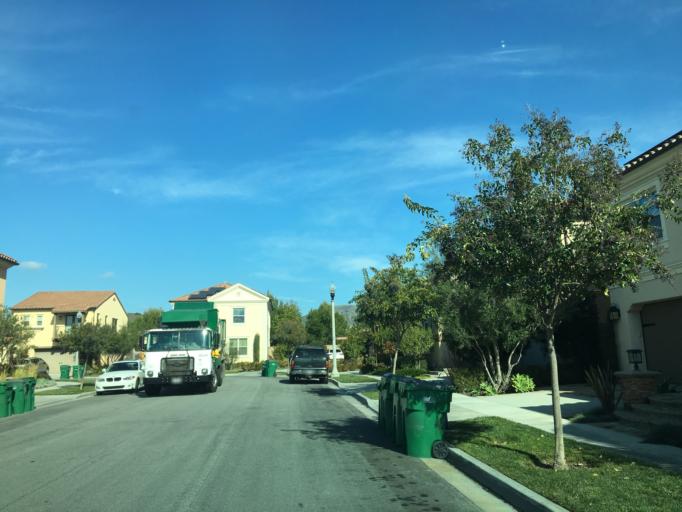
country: US
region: California
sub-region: Orange County
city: Lake Forest
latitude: 33.7052
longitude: -117.7366
